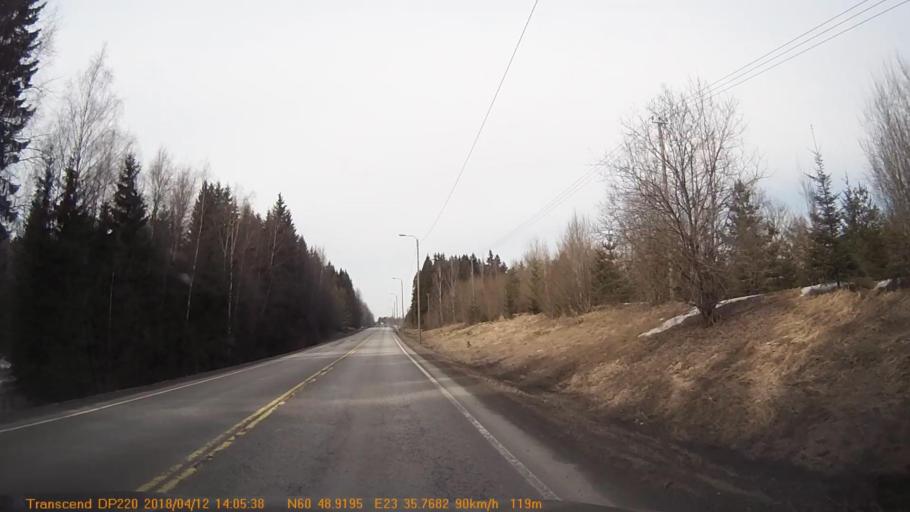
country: FI
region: Haeme
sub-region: Forssa
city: Forssa
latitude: 60.8157
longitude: 23.5958
